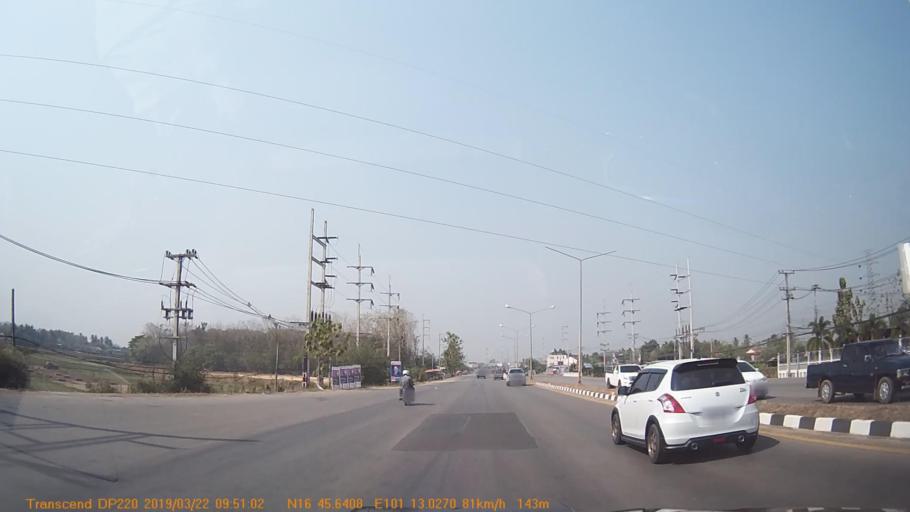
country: TH
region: Phetchabun
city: Lom Sak
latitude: 16.7604
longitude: 101.2168
